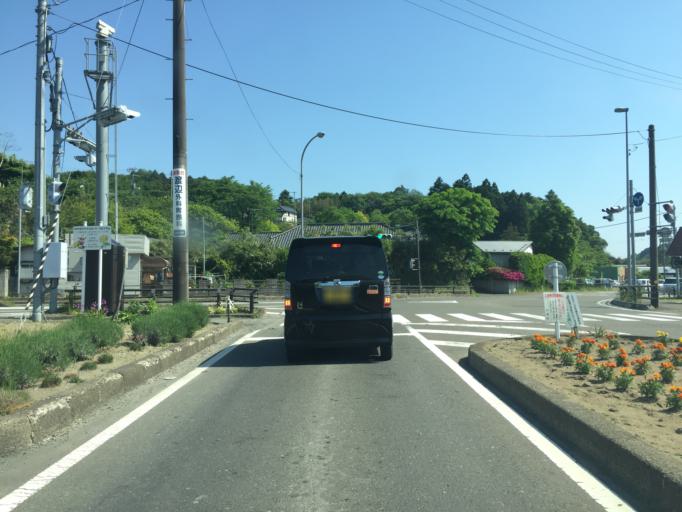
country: JP
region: Miyagi
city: Matsushima
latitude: 38.3997
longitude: 141.0679
